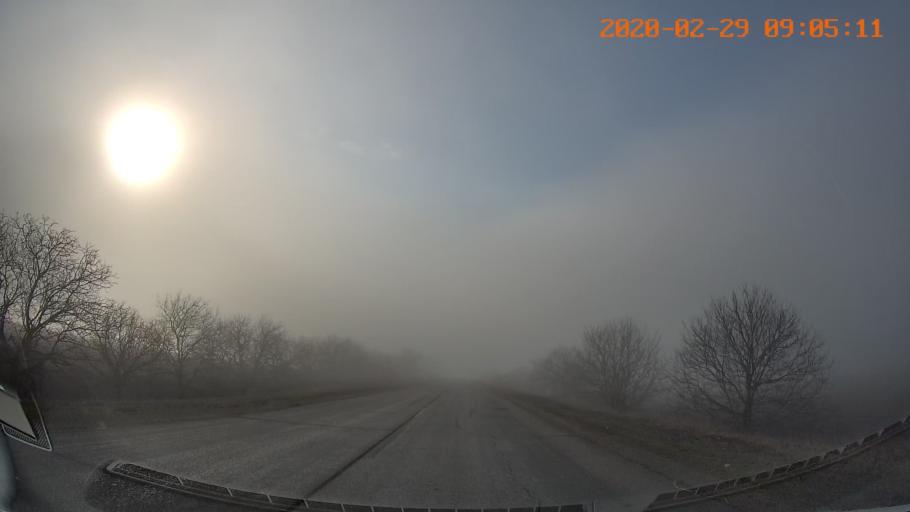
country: MD
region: Telenesti
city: Tiraspolul Nou
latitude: 46.8925
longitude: 29.7392
